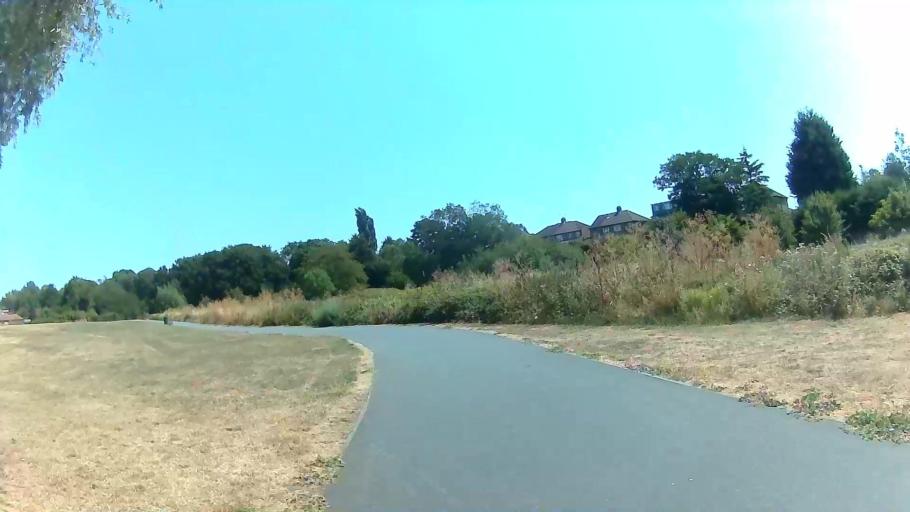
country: GB
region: England
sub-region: Greater London
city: Hornchurch
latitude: 51.5512
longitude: 0.2330
